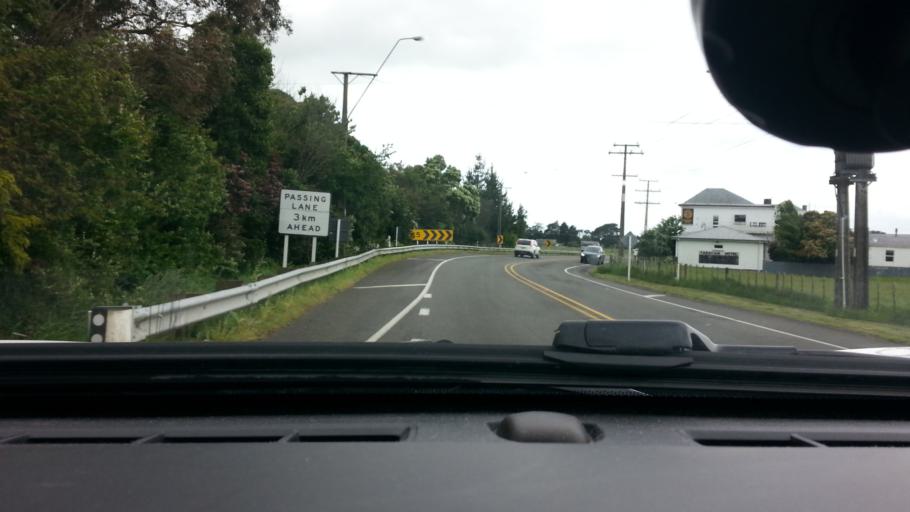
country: NZ
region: Wellington
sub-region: Masterton District
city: Masterton
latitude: -41.0154
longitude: 175.5362
